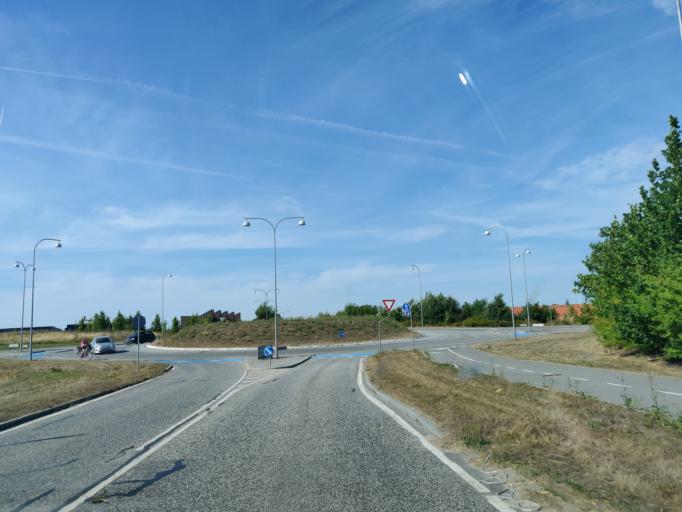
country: DK
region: Zealand
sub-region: Roskilde Kommune
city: Svogerslev
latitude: 55.6347
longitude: 12.0433
